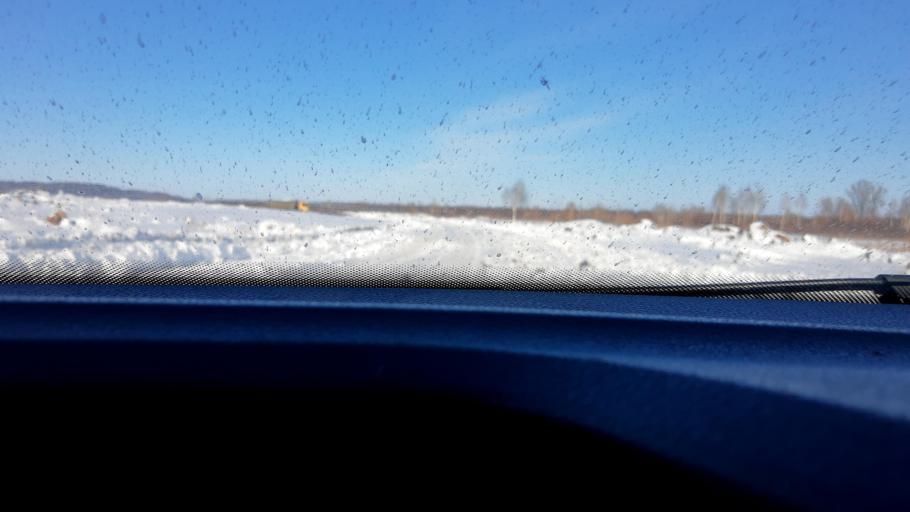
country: RU
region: Bashkortostan
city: Mikhaylovka
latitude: 54.7178
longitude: 55.8359
